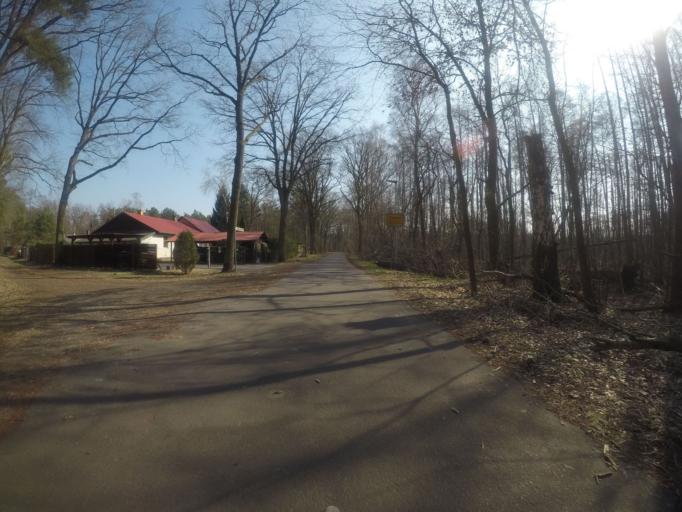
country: DE
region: Brandenburg
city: Bestensee
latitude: 52.2963
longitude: 13.7463
